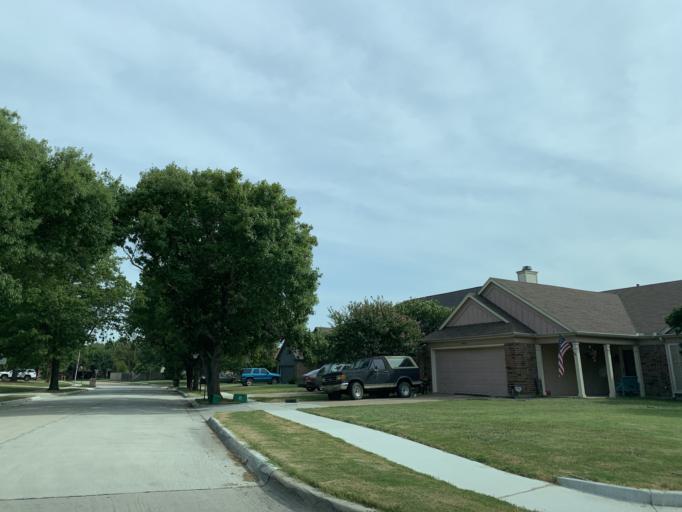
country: US
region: Texas
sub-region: Dallas County
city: Grand Prairie
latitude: 32.6630
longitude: -97.0040
